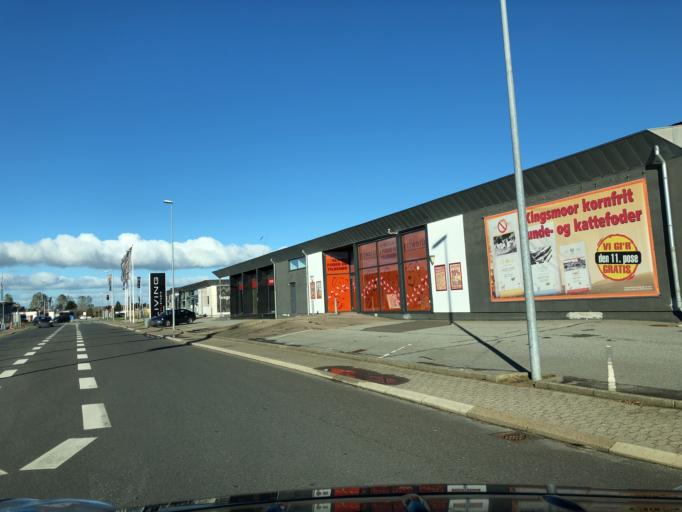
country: DK
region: Central Jutland
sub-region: Holstebro Kommune
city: Holstebro
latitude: 56.3772
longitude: 8.6203
